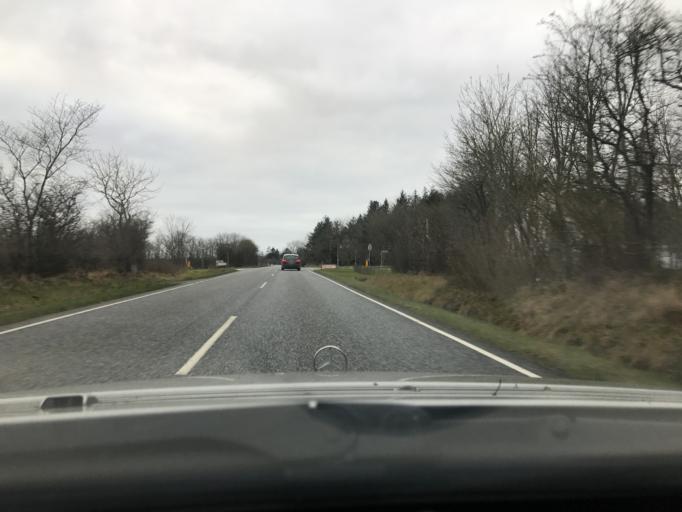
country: DK
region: South Denmark
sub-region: Tonder Kommune
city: Logumkloster
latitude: 55.1799
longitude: 8.9080
